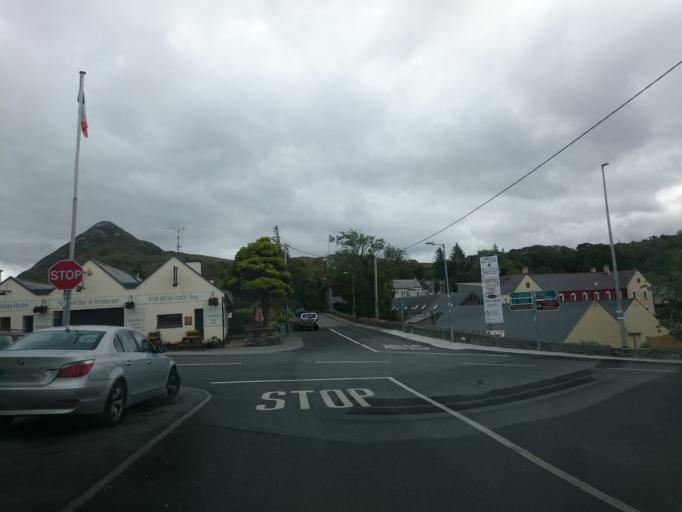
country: IE
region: Connaught
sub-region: County Galway
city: Clifden
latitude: 53.5537
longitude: -9.9485
